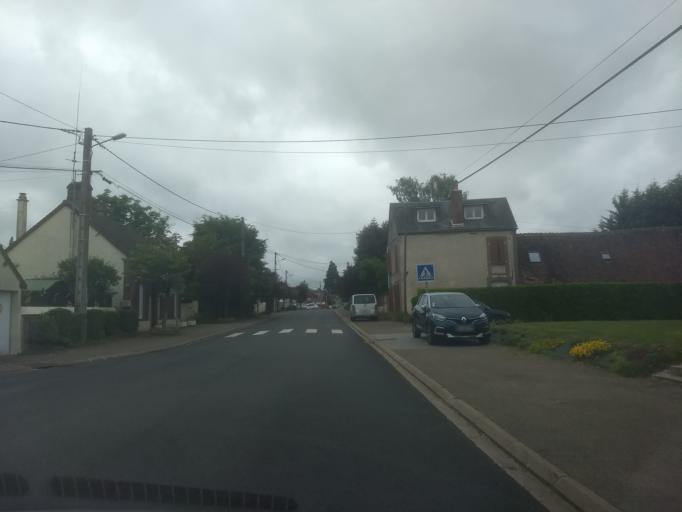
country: FR
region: Centre
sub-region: Departement d'Eure-et-Loir
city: La Loupe
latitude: 48.5041
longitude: 1.0219
